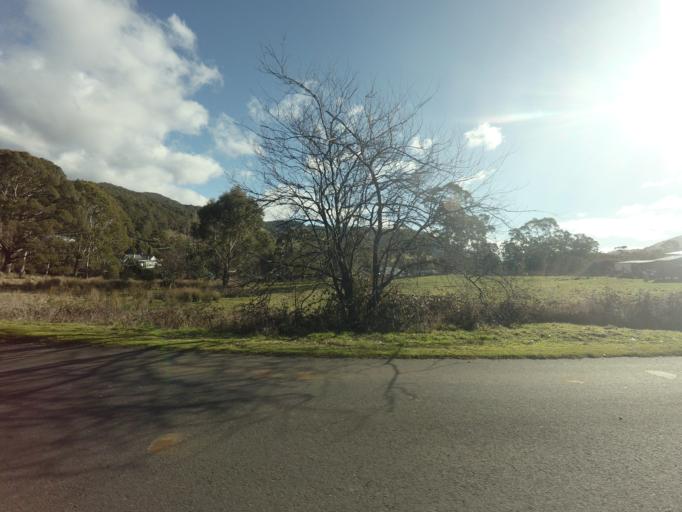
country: AU
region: Tasmania
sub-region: Glenorchy
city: Berriedale
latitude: -42.8429
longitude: 147.1945
